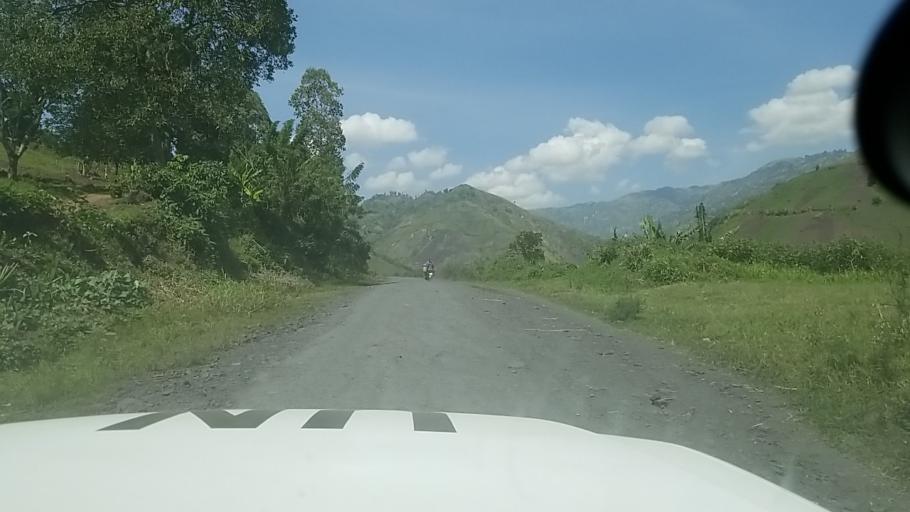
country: CD
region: Nord Kivu
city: Sake
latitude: -1.7399
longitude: 28.9991
